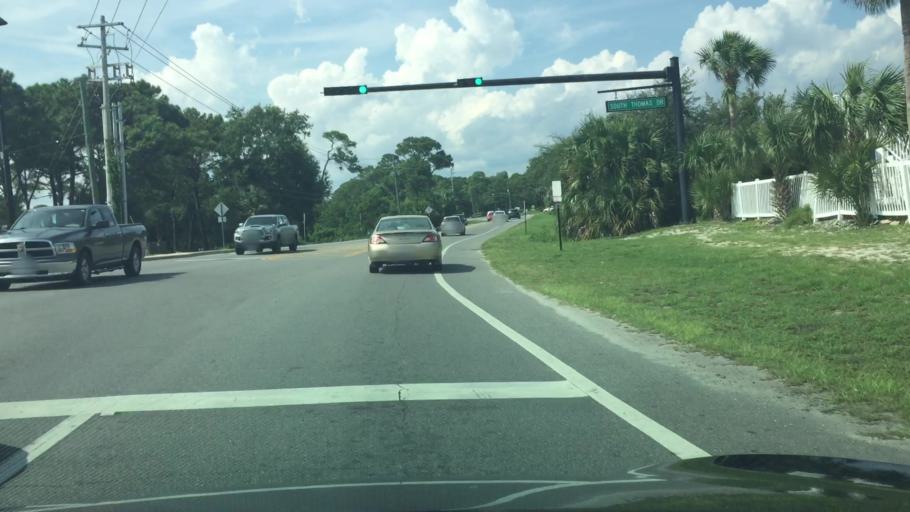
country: US
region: Florida
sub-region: Bay County
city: Panama City Beach
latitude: 30.1724
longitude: -85.7950
